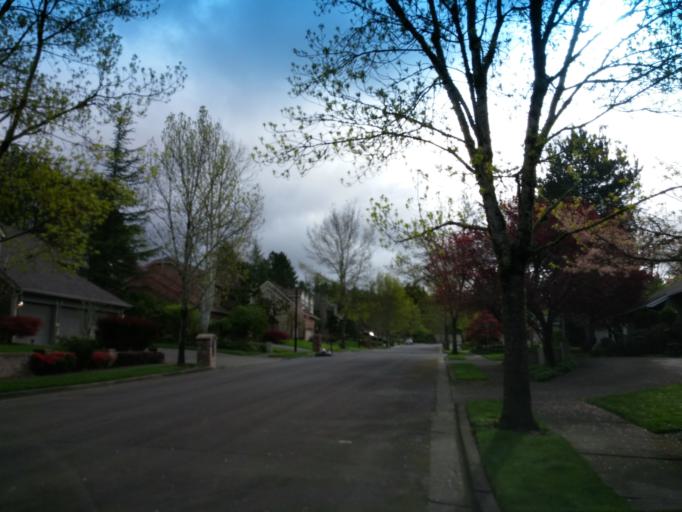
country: US
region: Oregon
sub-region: Washington County
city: Cedar Mill
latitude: 45.5384
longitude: -122.8147
